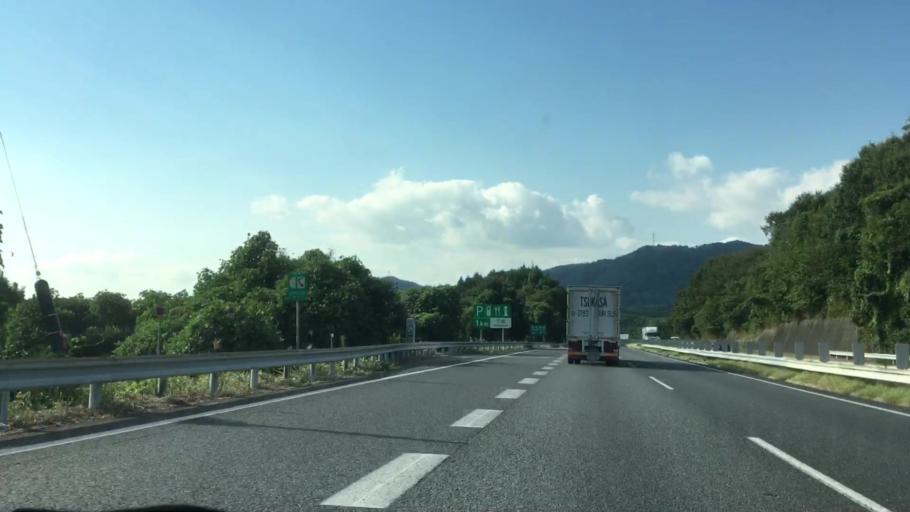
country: JP
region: Yamaguchi
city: Kudamatsu
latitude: 34.0356
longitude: 131.9277
